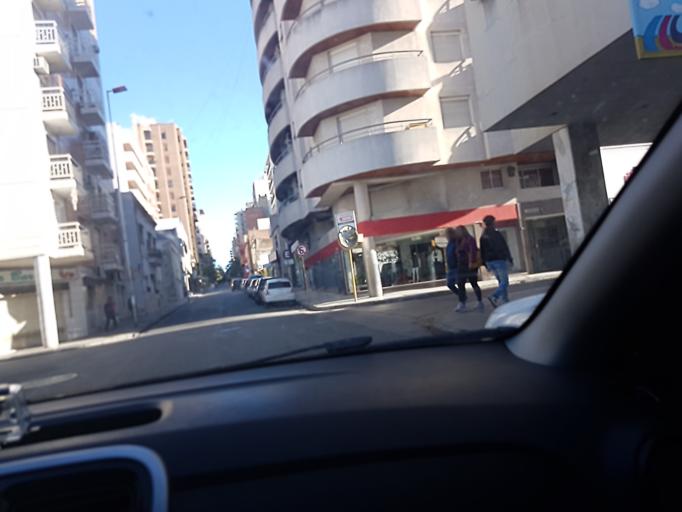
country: AR
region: Cordoba
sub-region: Departamento de Capital
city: Cordoba
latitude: -31.4212
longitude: -64.1788
